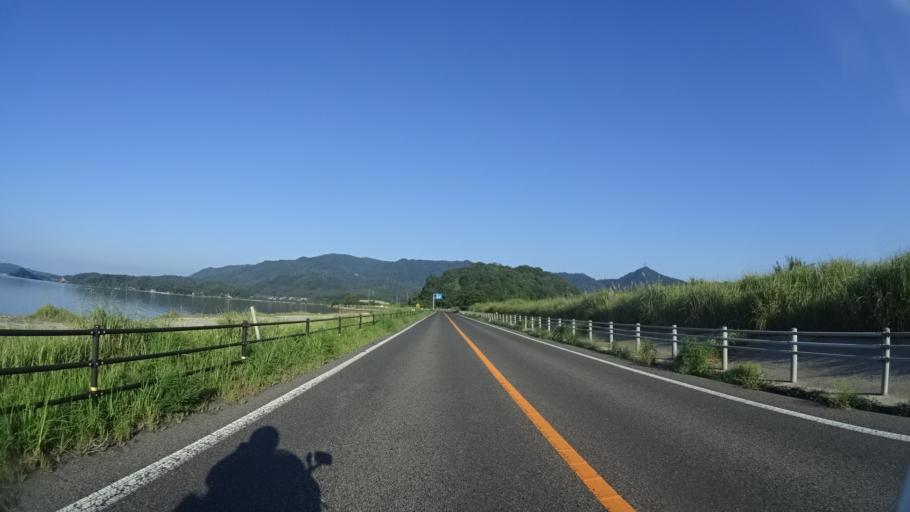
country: JP
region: Shimane
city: Sakaiminato
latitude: 35.5298
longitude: 133.1666
